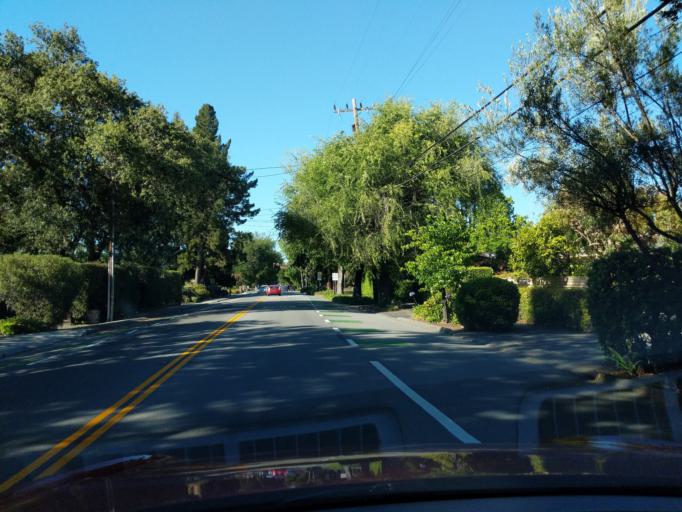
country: US
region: California
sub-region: San Mateo County
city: West Menlo Park
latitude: 37.4376
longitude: -122.1962
